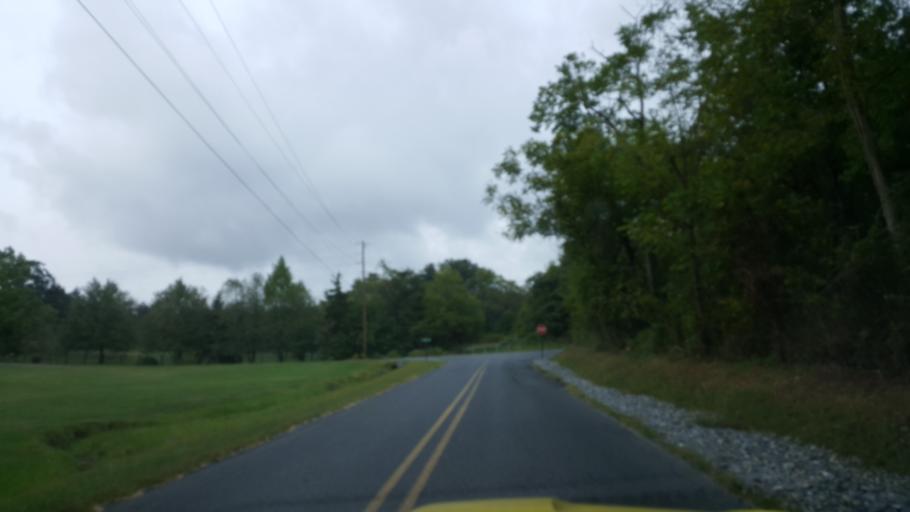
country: US
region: Pennsylvania
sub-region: Lebanon County
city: Campbelltown
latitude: 40.2445
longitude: -76.5266
